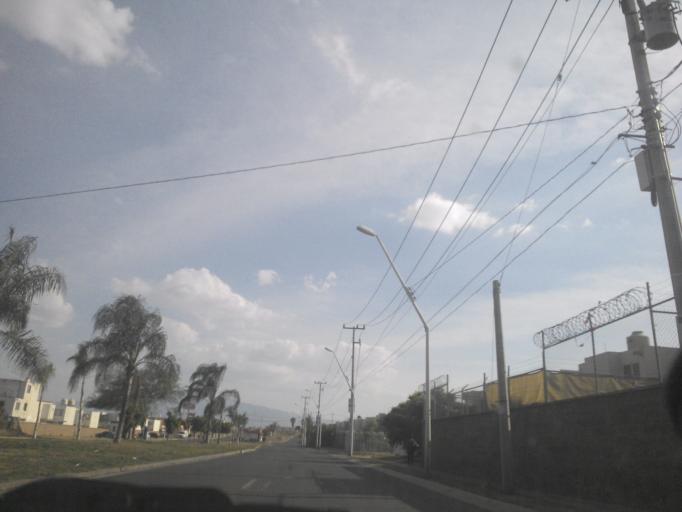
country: MX
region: Jalisco
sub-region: San Pedro Tlaquepaque
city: Paseo del Prado
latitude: 20.5782
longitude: -103.3881
